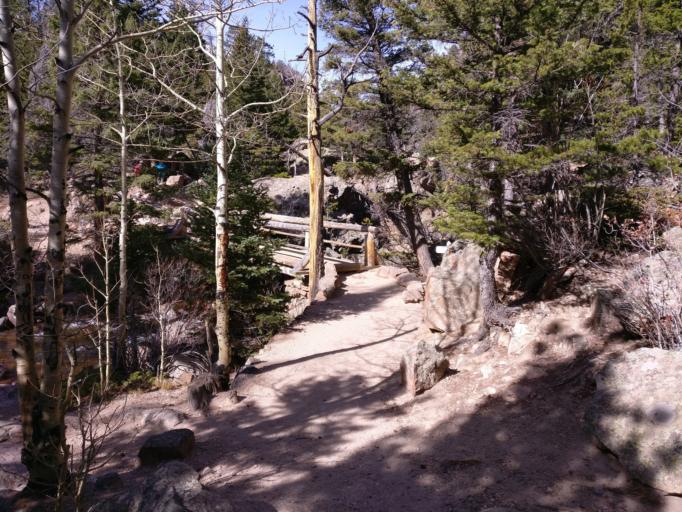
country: US
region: Colorado
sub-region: Larimer County
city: Estes Park
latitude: 40.3494
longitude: -105.6594
